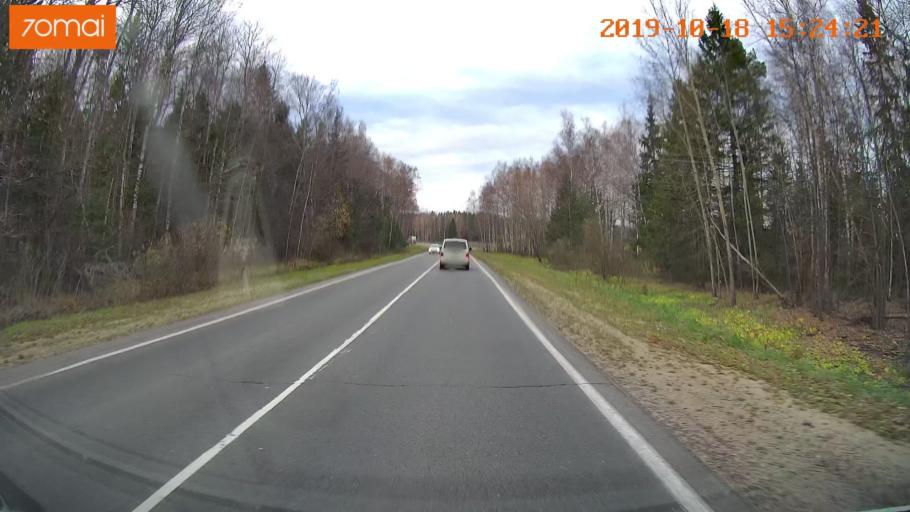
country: RU
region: Vladimir
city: Anopino
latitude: 55.7334
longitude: 40.7239
